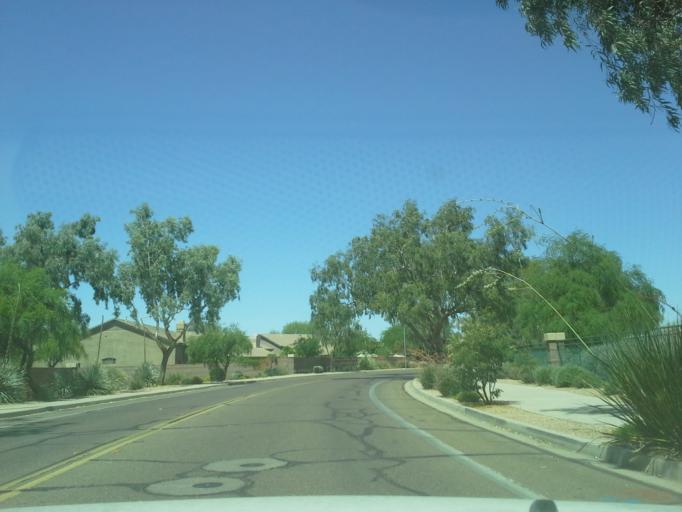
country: US
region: Arizona
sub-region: Maricopa County
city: Paradise Valley
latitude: 33.6183
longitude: -111.9387
